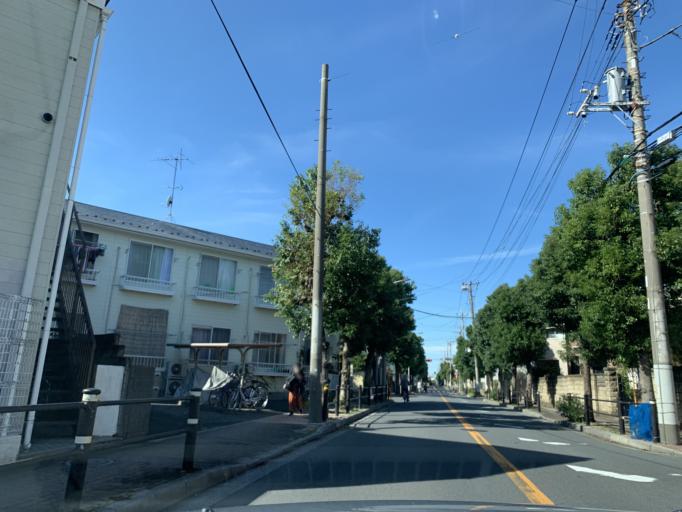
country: JP
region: Chiba
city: Matsudo
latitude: 35.7278
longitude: 139.9247
